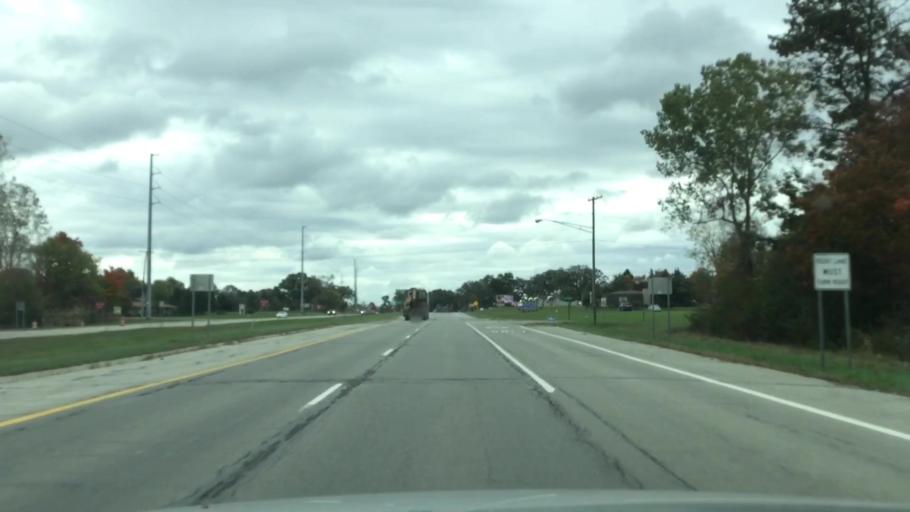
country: US
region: Michigan
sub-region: Oakland County
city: Milford
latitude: 42.6353
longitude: -83.7149
